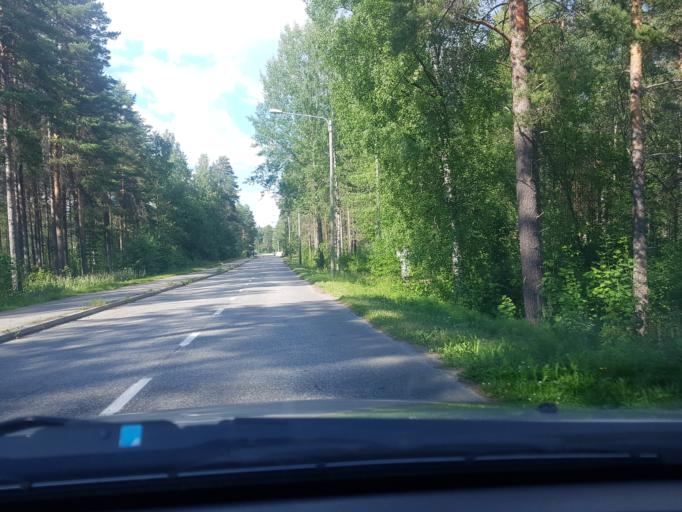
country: FI
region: Kainuu
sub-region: Kehys-Kainuu
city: Kuhmo
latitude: 64.1305
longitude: 29.5441
